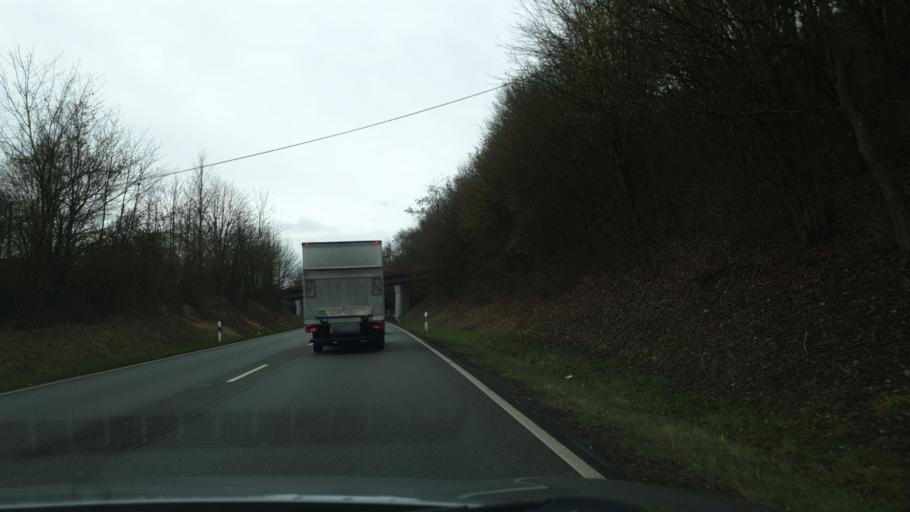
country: DE
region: Rheinland-Pfalz
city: Rhens
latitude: 50.2866
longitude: 7.6088
